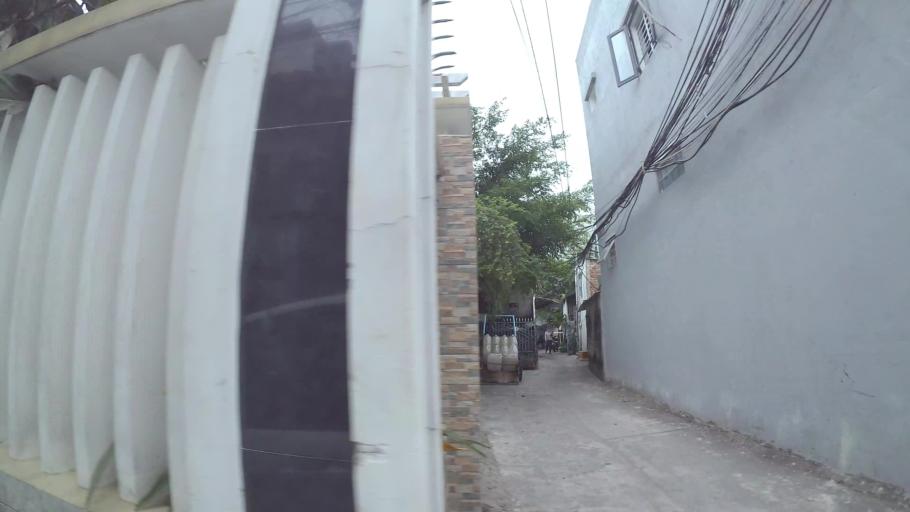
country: VN
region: Da Nang
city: Son Tra
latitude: 16.0602
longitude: 108.2315
